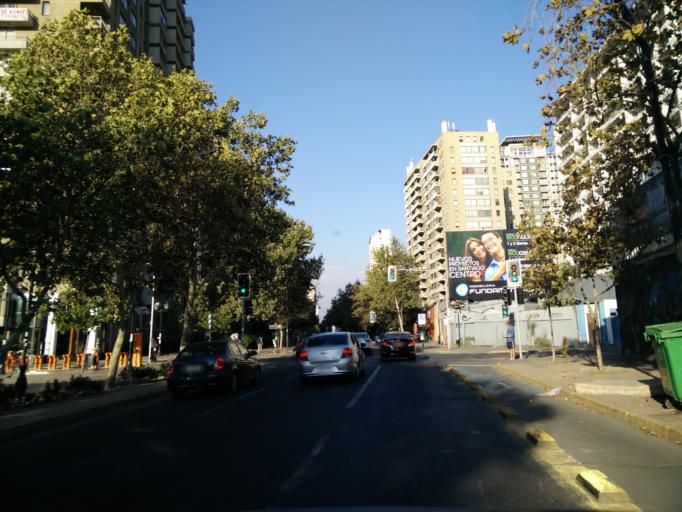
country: CL
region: Santiago Metropolitan
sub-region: Provincia de Santiago
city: Santiago
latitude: -33.4504
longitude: -70.6434
